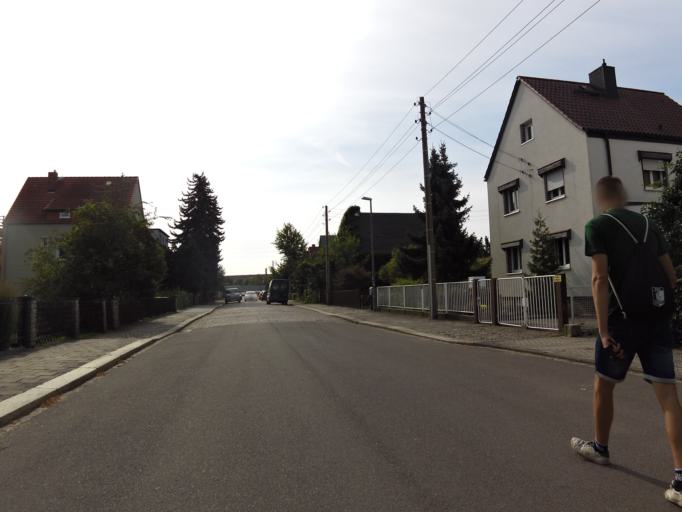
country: DE
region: Saxony
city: Leipzig
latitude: 51.3569
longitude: 12.3057
